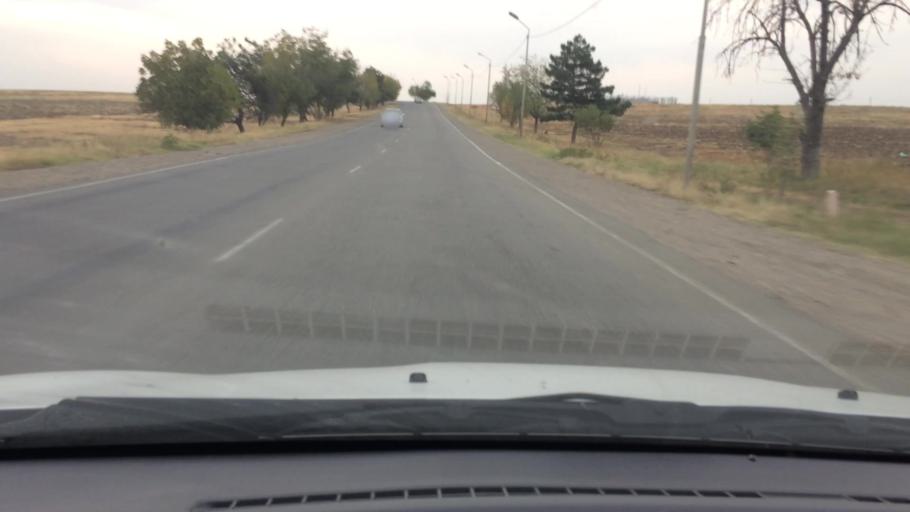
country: GE
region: Kvemo Kartli
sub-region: Marneuli
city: Marneuli
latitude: 41.5191
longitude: 44.7816
